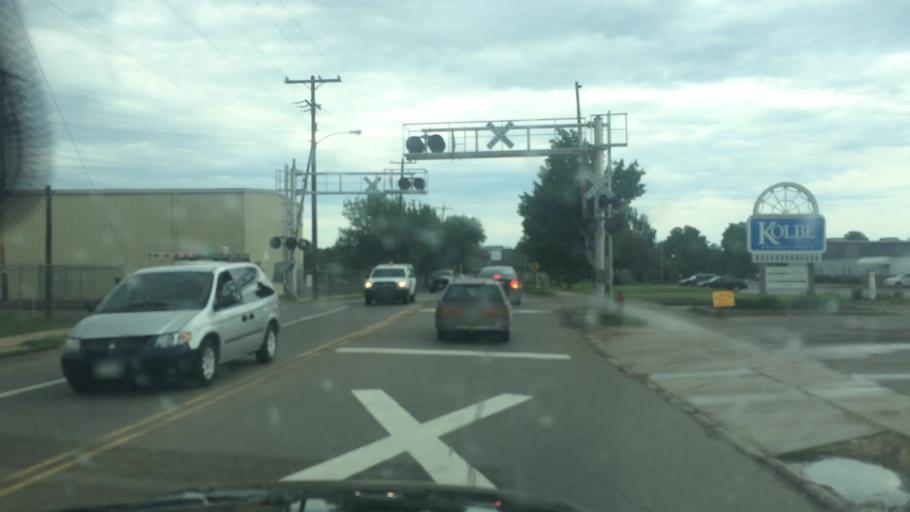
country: US
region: Wisconsin
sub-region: Marathon County
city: Wausau
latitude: 44.9484
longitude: -89.6378
